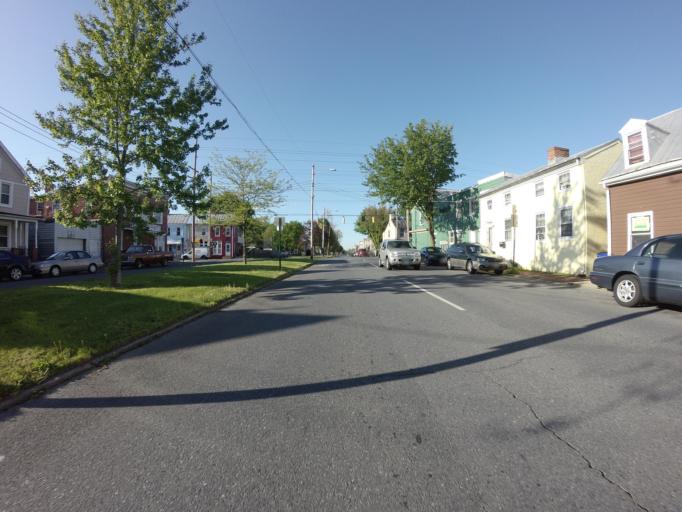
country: US
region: Maryland
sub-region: Frederick County
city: Frederick
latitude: 39.4201
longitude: -77.4128
